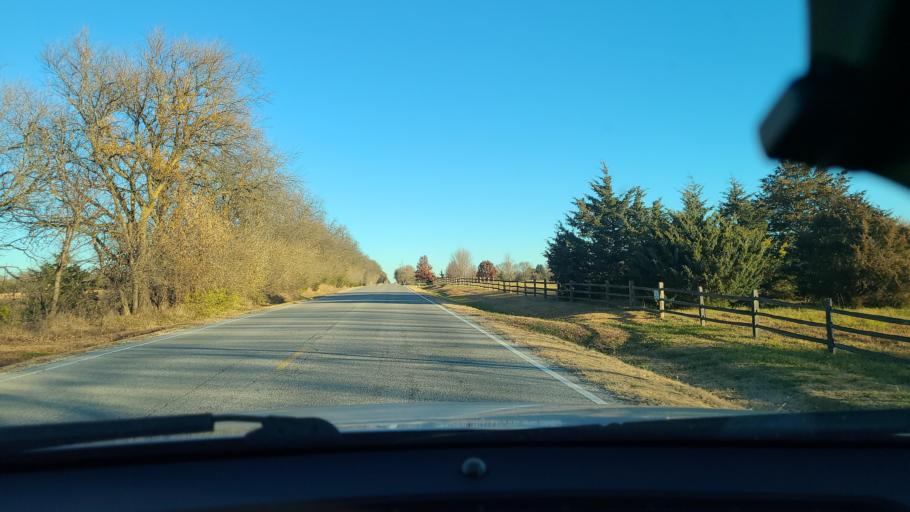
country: US
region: Kansas
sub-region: Sedgwick County
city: Park City
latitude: 37.8462
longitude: -97.3174
